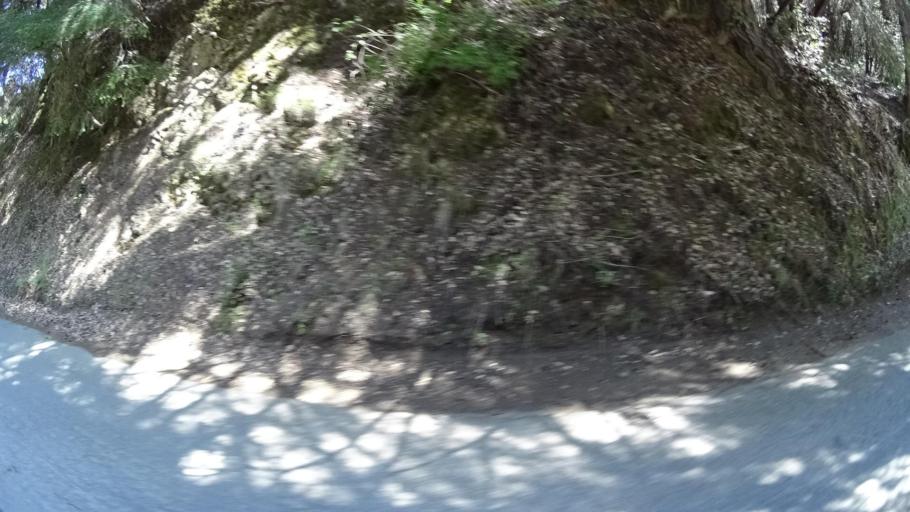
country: US
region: California
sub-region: Humboldt County
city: Redway
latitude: 40.1053
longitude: -123.9538
